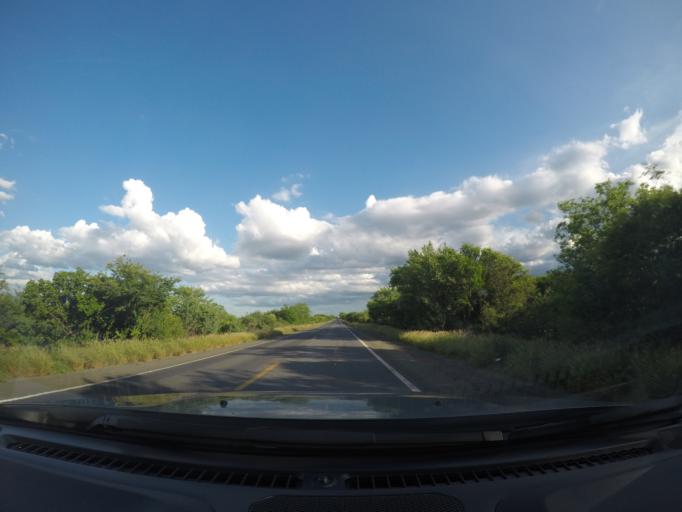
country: BR
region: Bahia
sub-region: Oliveira Dos Brejinhos
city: Beira Rio
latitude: -12.2296
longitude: -42.7824
